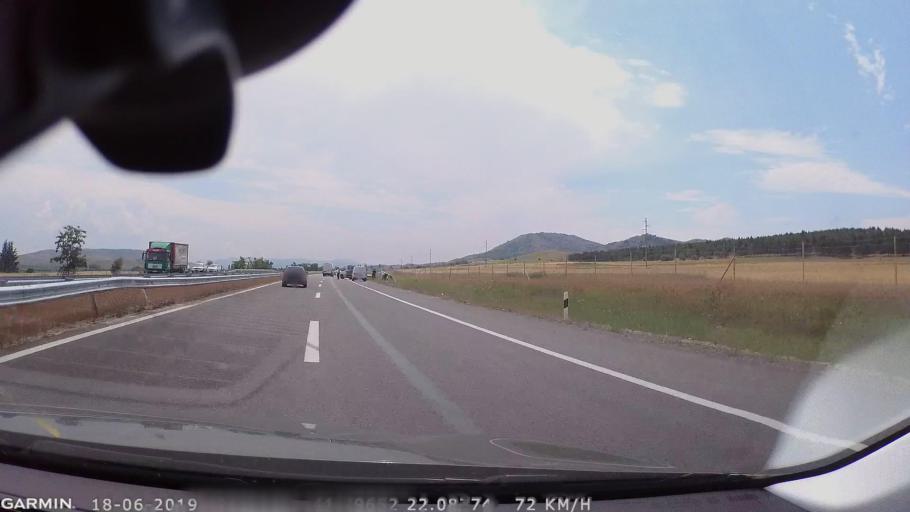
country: MK
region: Stip
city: Shtip
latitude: 41.7962
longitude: 22.0887
